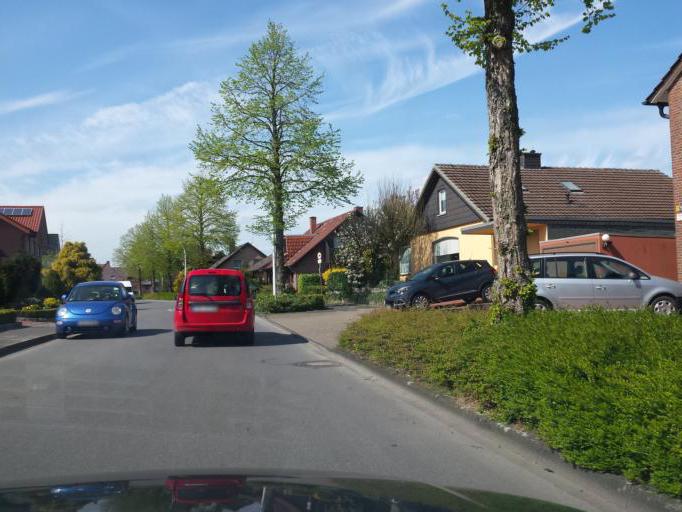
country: DE
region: North Rhine-Westphalia
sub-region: Regierungsbezirk Munster
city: Nottuln
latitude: 51.9221
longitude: 7.3592
